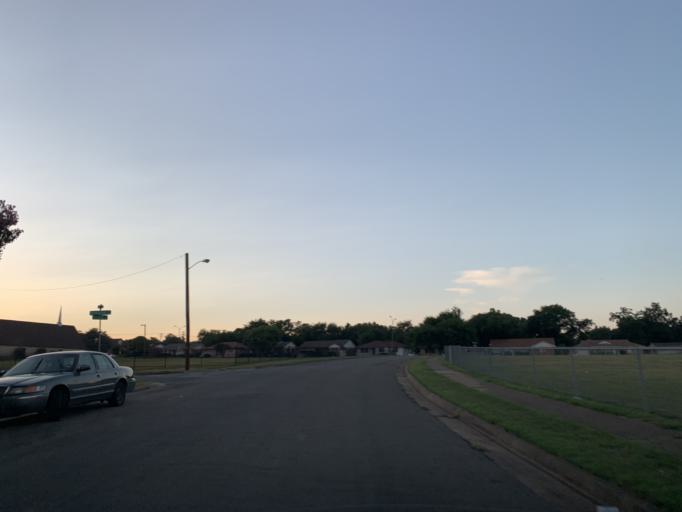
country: US
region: Texas
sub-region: Dallas County
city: Hutchins
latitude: 32.6737
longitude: -96.7991
